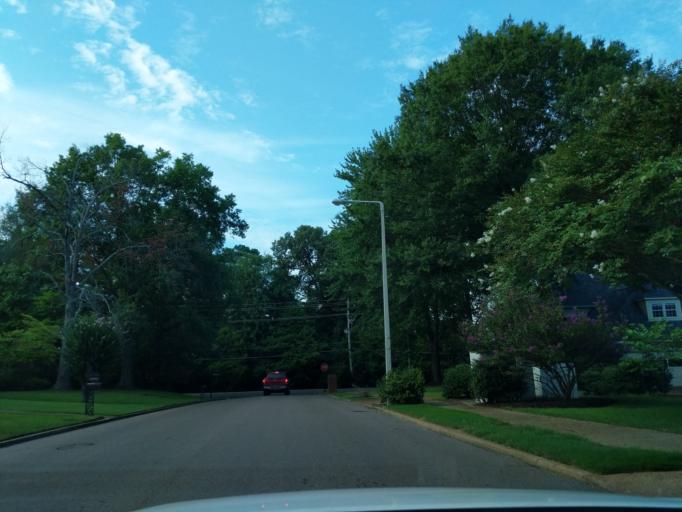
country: US
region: Tennessee
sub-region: Shelby County
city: Germantown
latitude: 35.0725
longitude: -89.7869
